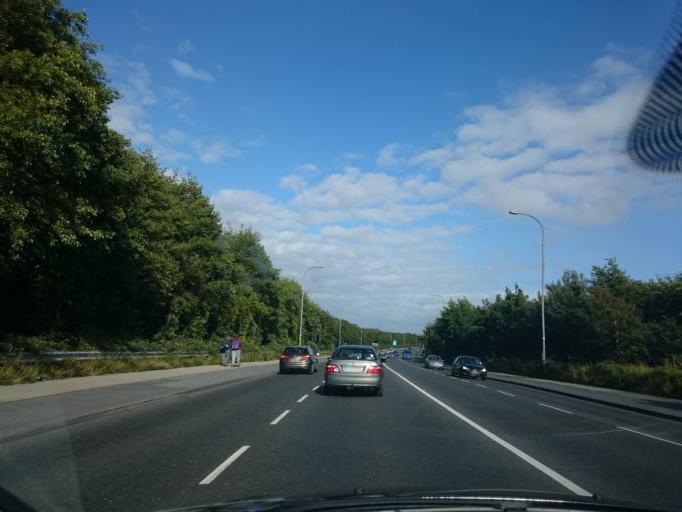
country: IE
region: Connaught
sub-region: County Galway
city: Gaillimh
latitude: 53.2829
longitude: -9.0576
